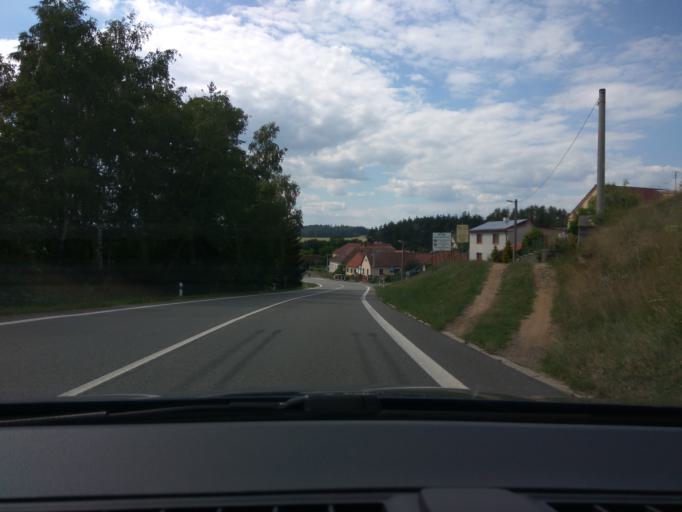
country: CZ
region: Jihocesky
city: Kovarov
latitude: 49.4733
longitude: 14.2945
